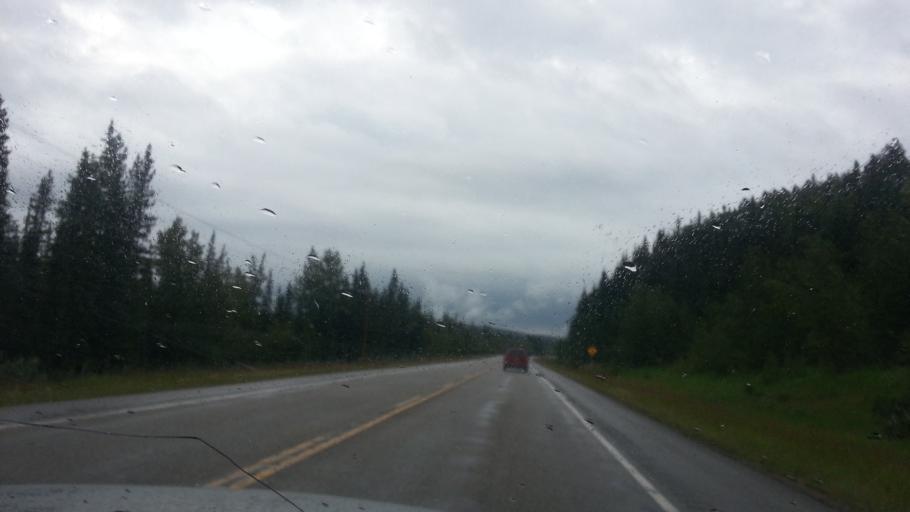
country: CA
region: Alberta
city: Cochrane
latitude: 50.9155
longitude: -114.6175
